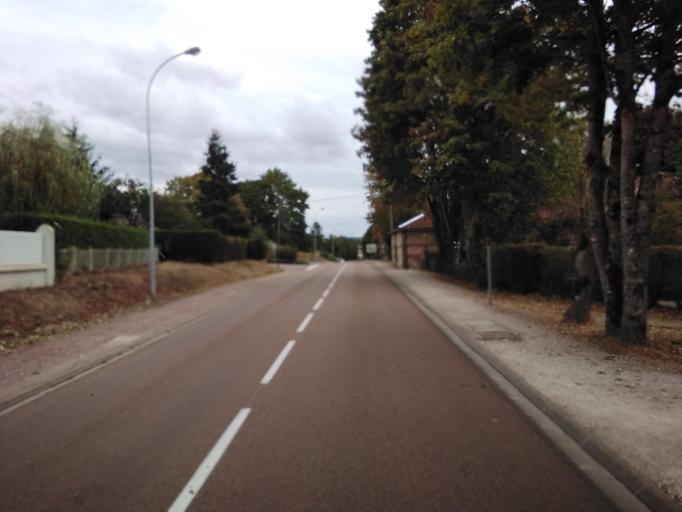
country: FR
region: Champagne-Ardenne
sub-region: Departement de l'Aube
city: Bar-sur-Seine
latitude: 48.1198
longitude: 4.3845
